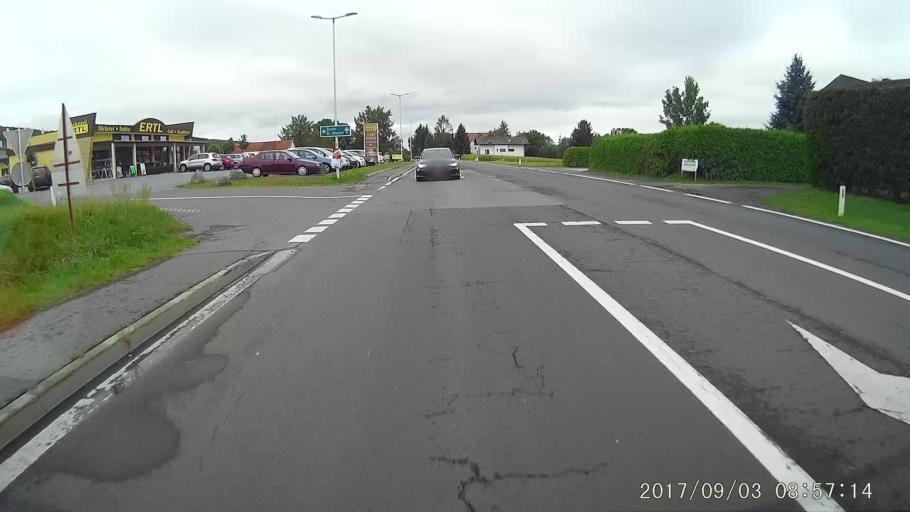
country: AT
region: Styria
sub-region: Politischer Bezirk Suedoststeiermark
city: Merkendorf
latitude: 46.8594
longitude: 15.9022
